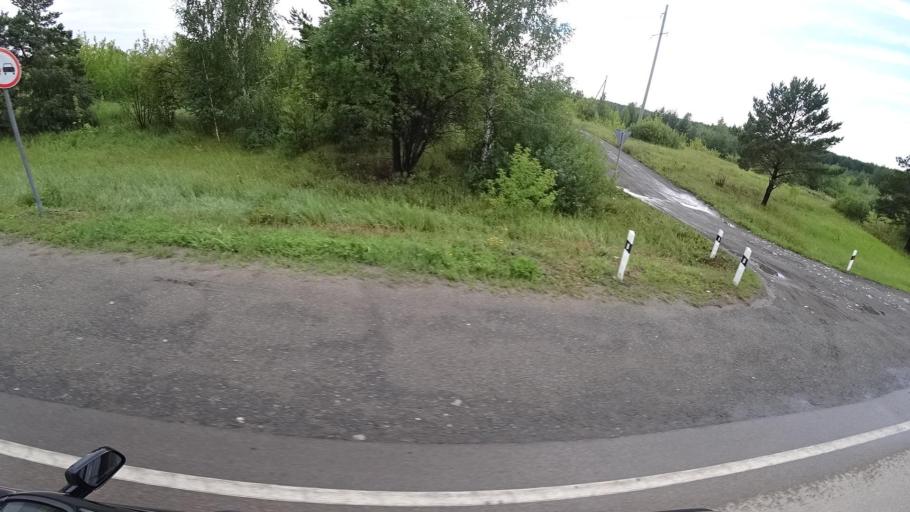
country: RU
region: Sverdlovsk
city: Kamyshlov
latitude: 56.8416
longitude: 62.7852
